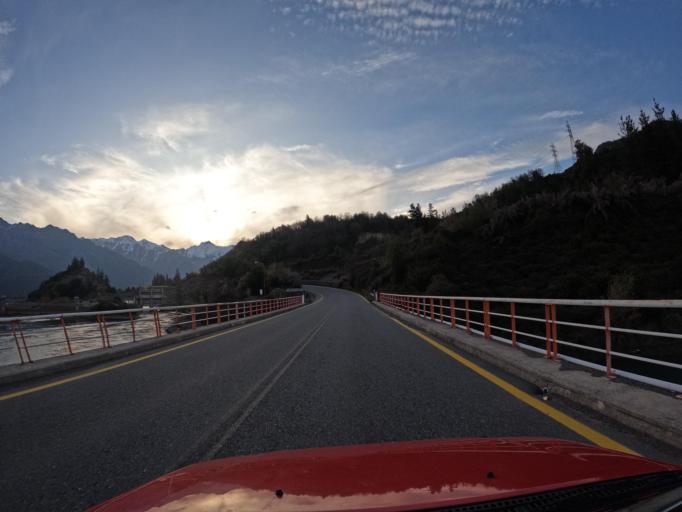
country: CL
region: Maule
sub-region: Provincia de Linares
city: Colbun
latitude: -35.8076
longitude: -70.9462
